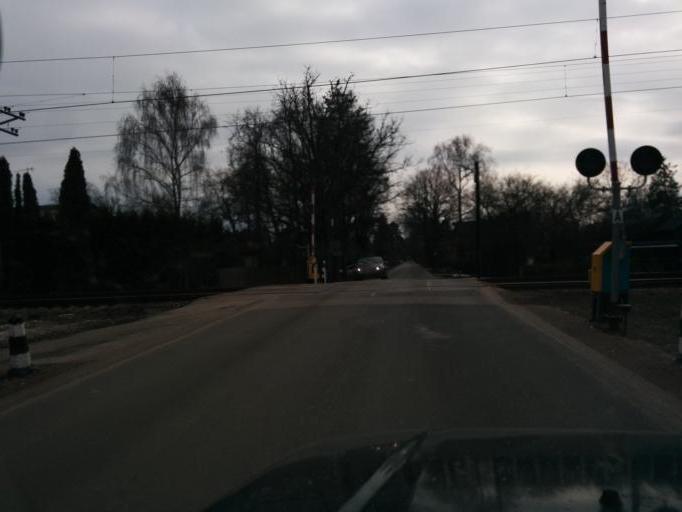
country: LV
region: Jurmala
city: Jurmala
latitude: 56.9595
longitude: 23.7228
